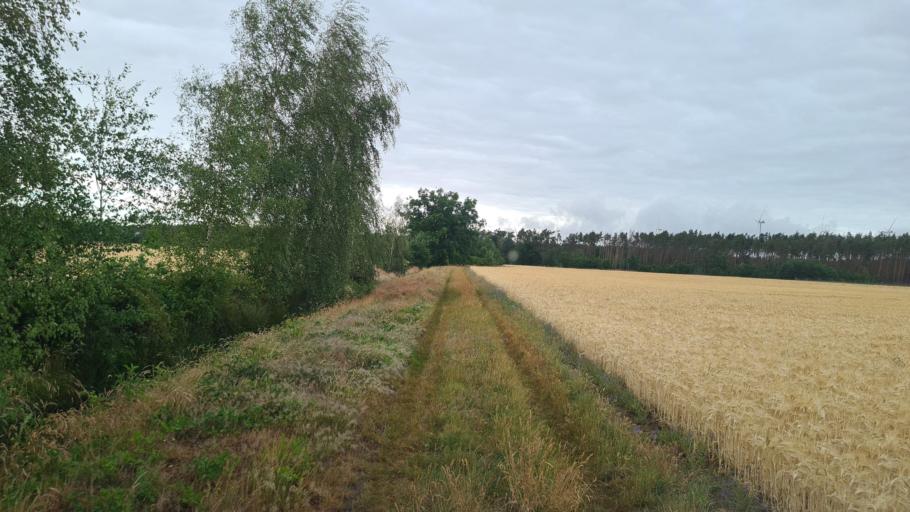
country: DE
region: Brandenburg
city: Bad Liebenwerda
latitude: 51.4992
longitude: 13.3115
